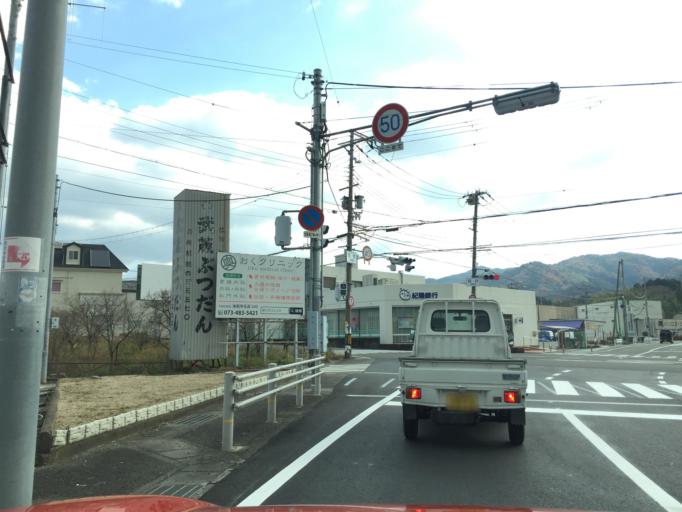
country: JP
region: Wakayama
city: Kainan
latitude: 34.1604
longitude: 135.2671
